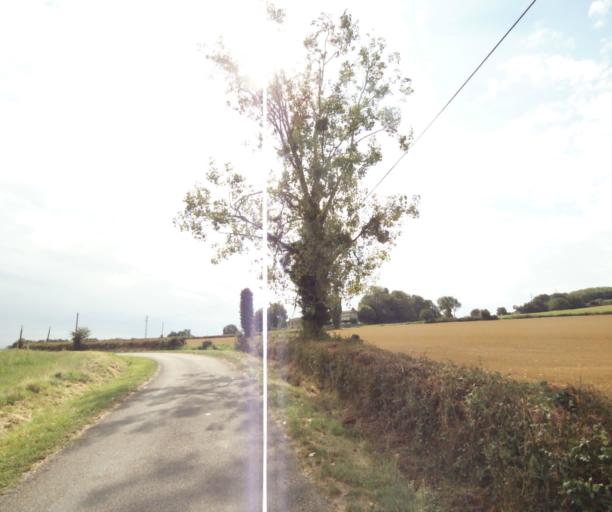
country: FR
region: Bourgogne
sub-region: Departement de Saone-et-Loire
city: Tournus
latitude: 46.5462
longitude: 4.9115
